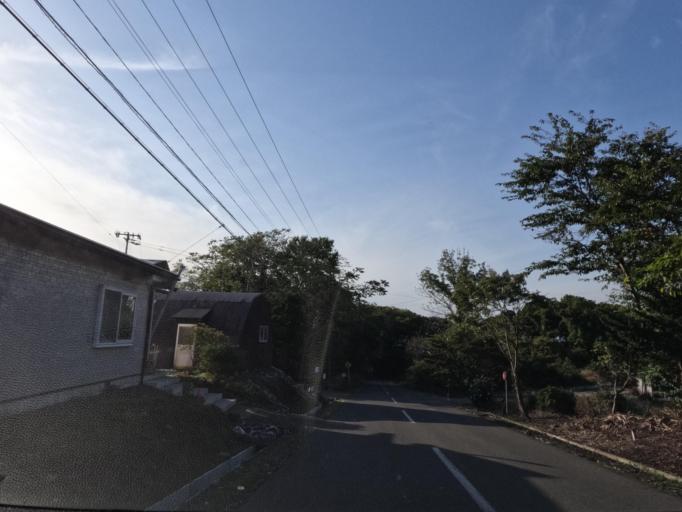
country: JP
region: Hokkaido
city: Date
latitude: 42.4101
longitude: 140.9170
